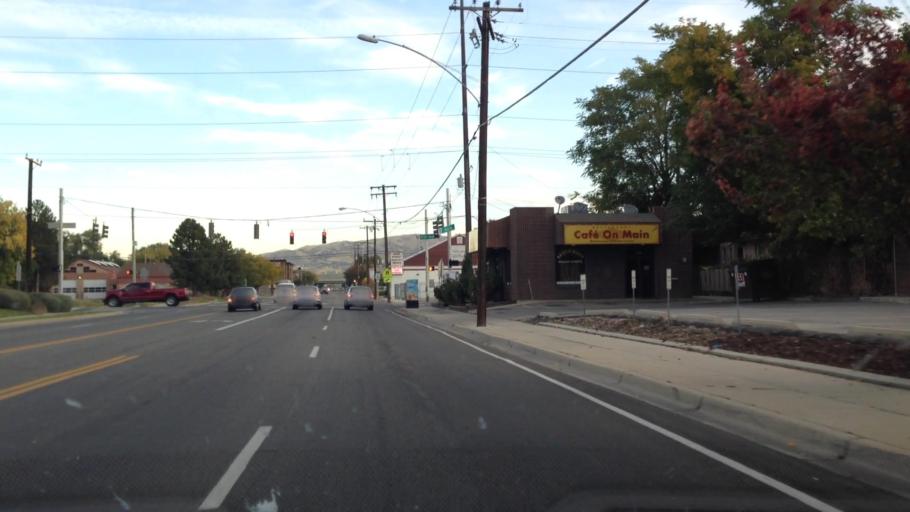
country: US
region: Utah
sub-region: Salt Lake County
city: South Salt Lake
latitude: 40.7120
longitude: -111.8911
